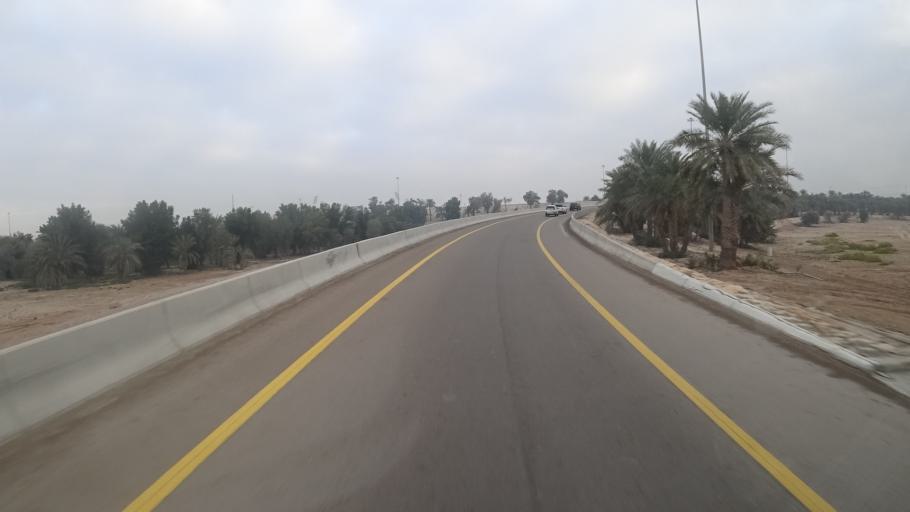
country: AE
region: Abu Dhabi
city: Abu Dhabi
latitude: 24.3877
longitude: 54.5431
